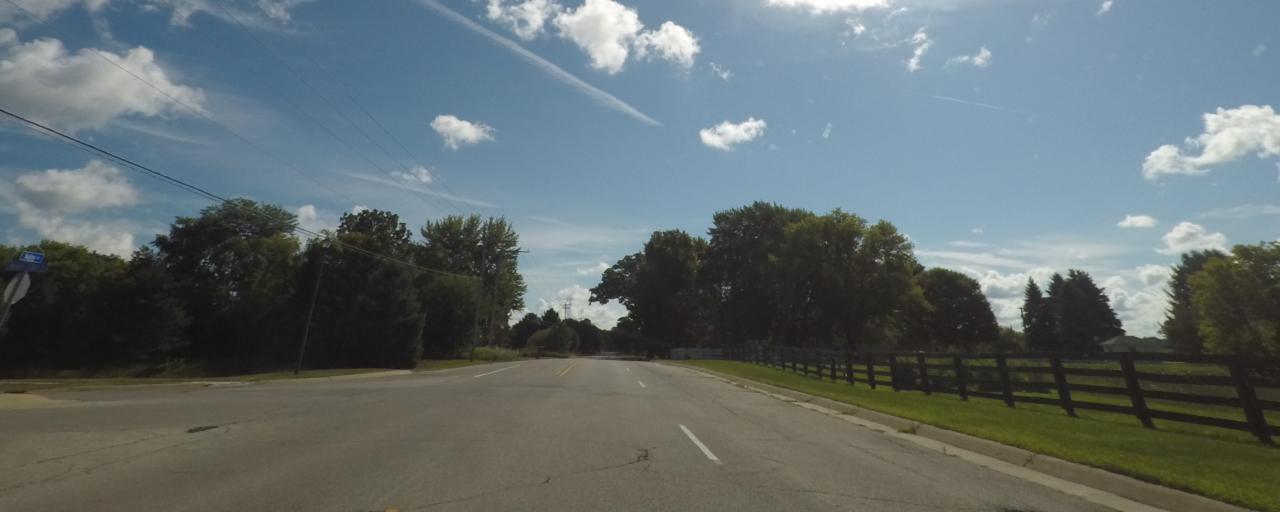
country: US
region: Wisconsin
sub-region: Waukesha County
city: Oconomowoc
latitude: 43.0831
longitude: -88.5313
